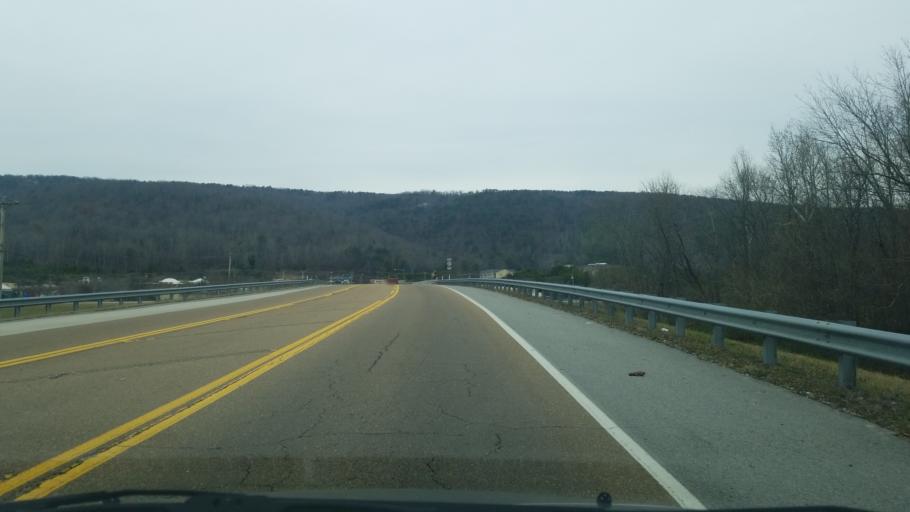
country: US
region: Tennessee
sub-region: Hamilton County
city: Soddy-Daisy
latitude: 35.2337
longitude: -85.1953
